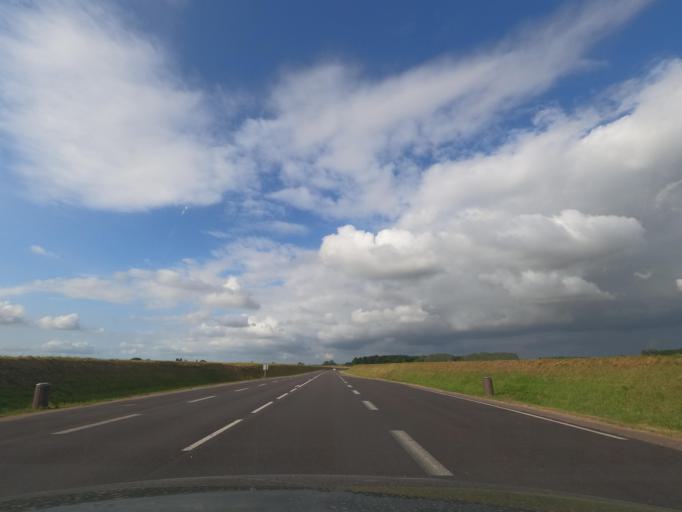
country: FR
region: Haute-Normandie
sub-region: Departement de l'Eure
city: Bernay
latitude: 49.1010
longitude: 0.5756
